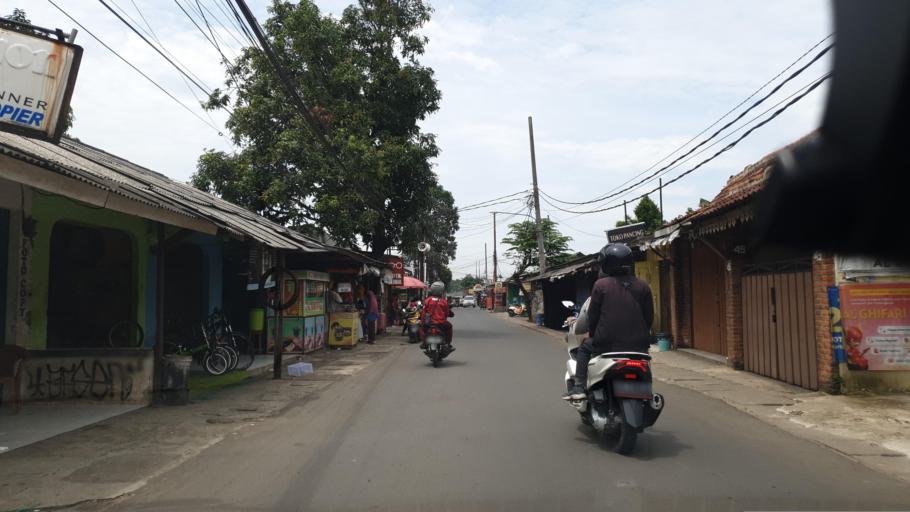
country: ID
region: West Java
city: Pamulang
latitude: -6.3678
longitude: 106.7557
